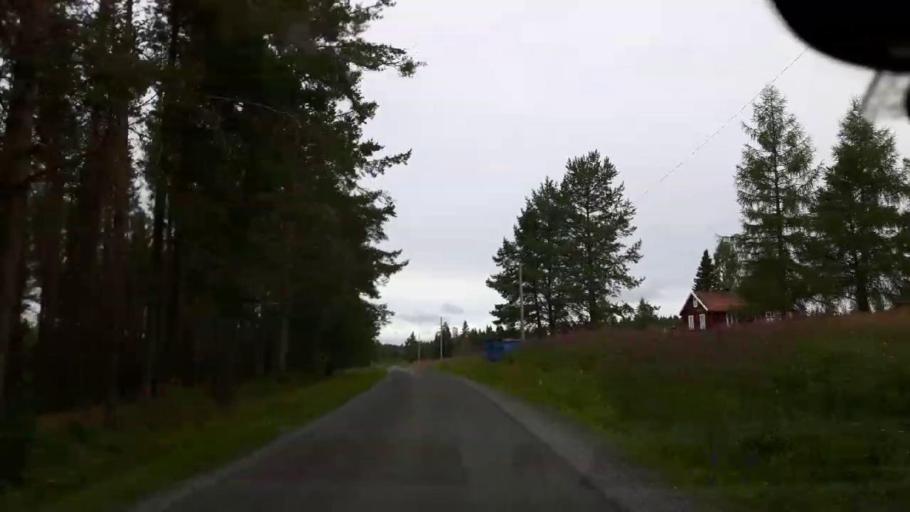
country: SE
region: Jaemtland
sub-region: Krokoms Kommun
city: Krokom
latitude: 63.2753
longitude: 14.3997
